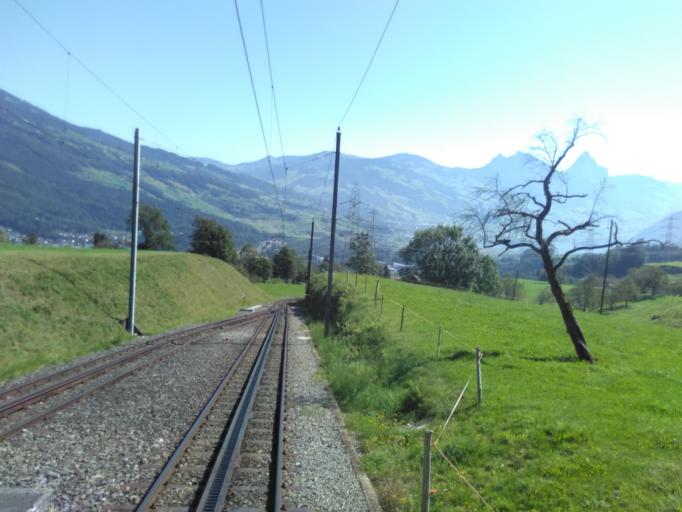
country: CH
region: Schwyz
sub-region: Bezirk Schwyz
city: Goldau
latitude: 47.0404
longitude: 8.5313
